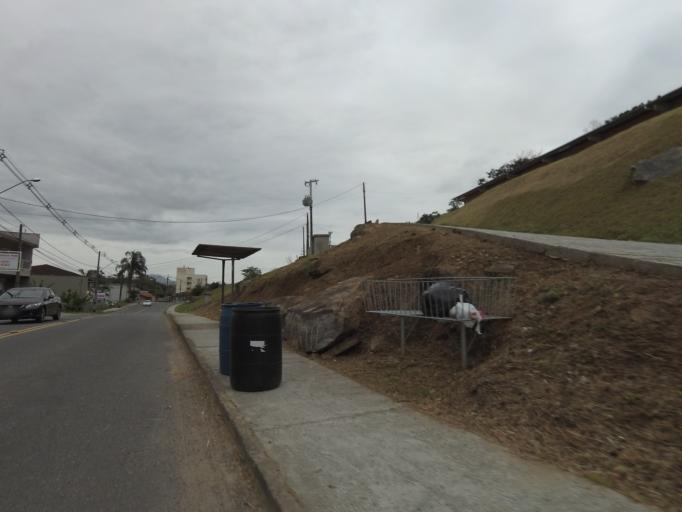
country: BR
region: Santa Catarina
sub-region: Blumenau
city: Blumenau
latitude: -26.8996
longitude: -49.1270
